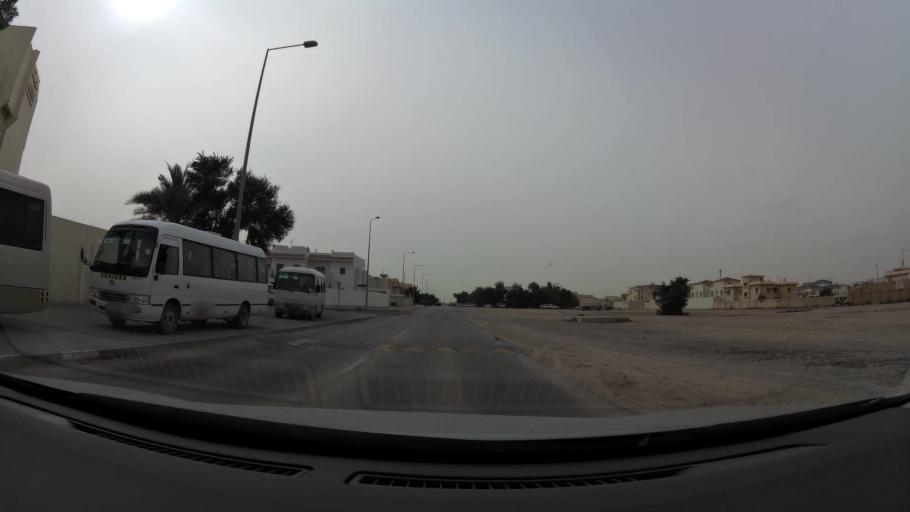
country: QA
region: Baladiyat ad Dawhah
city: Doha
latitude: 25.2462
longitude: 51.5048
